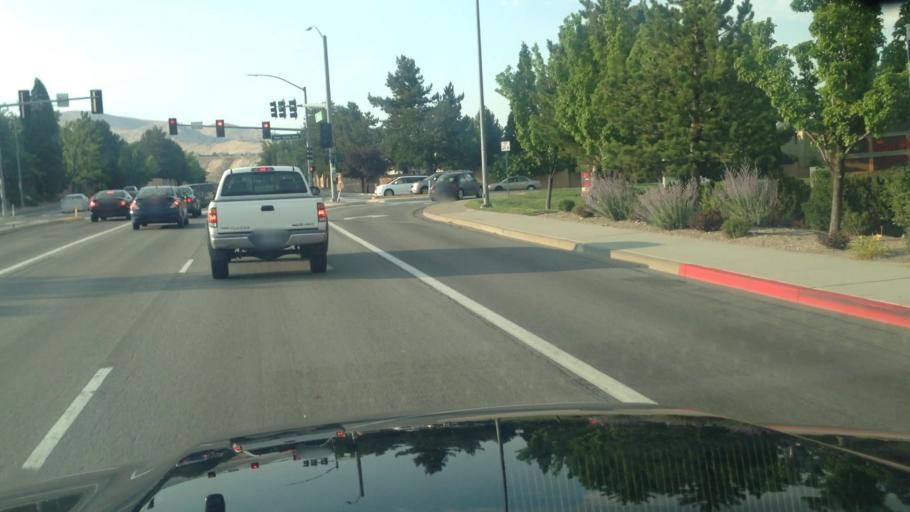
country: US
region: Nevada
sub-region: Washoe County
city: Mogul
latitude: 39.5290
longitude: -119.8820
